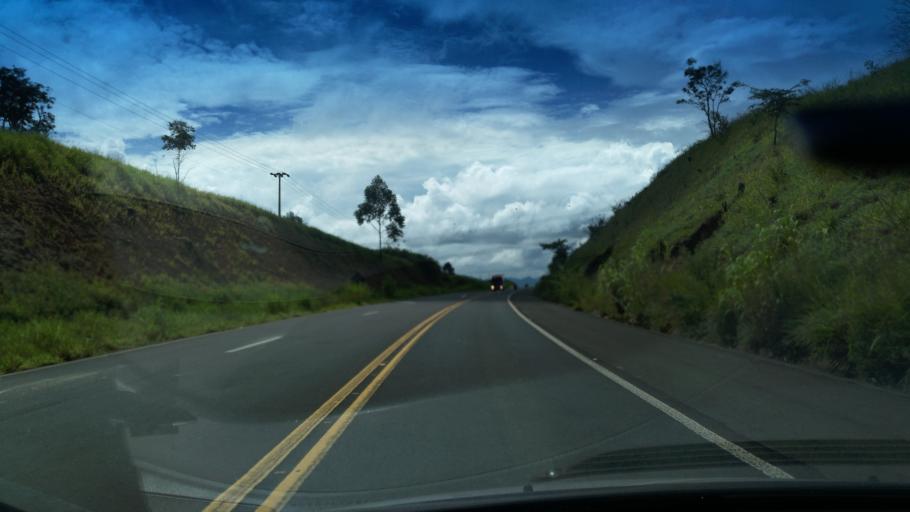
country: BR
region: Sao Paulo
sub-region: Santo Antonio Do Jardim
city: Espirito Santo do Pinhal
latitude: -22.1407
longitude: -46.7105
